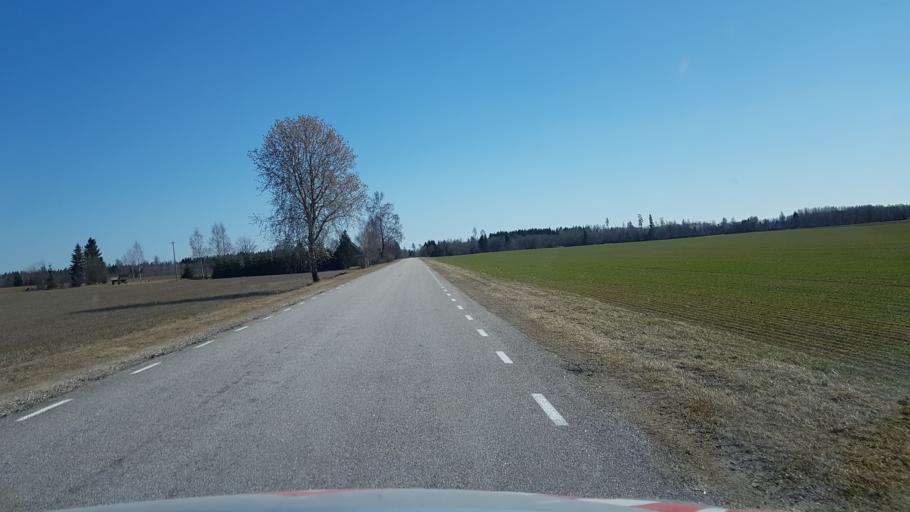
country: EE
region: Laeaene-Virumaa
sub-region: Vaeike-Maarja vald
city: Vaike-Maarja
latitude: 59.1024
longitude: 26.3914
